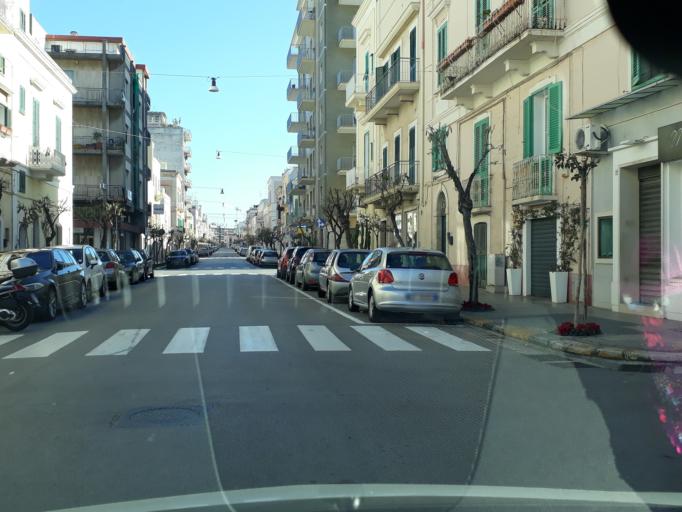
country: IT
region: Apulia
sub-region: Provincia di Bari
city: Monopoli
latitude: 40.9530
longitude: 17.2983
